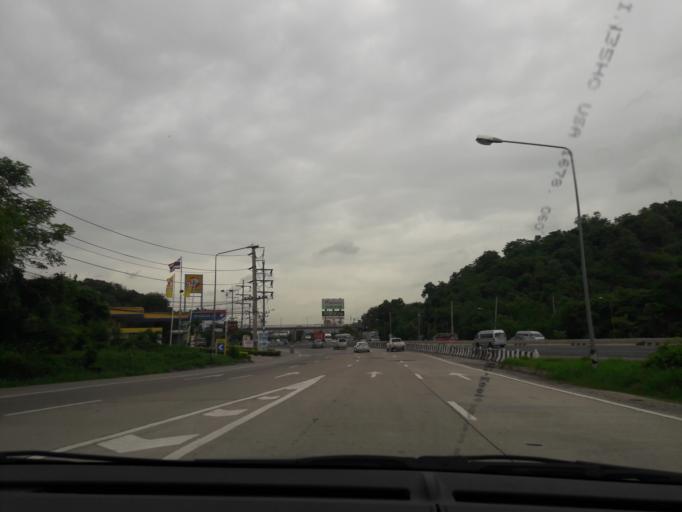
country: TH
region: Sara Buri
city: Saraburi
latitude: 14.5425
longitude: 100.9548
